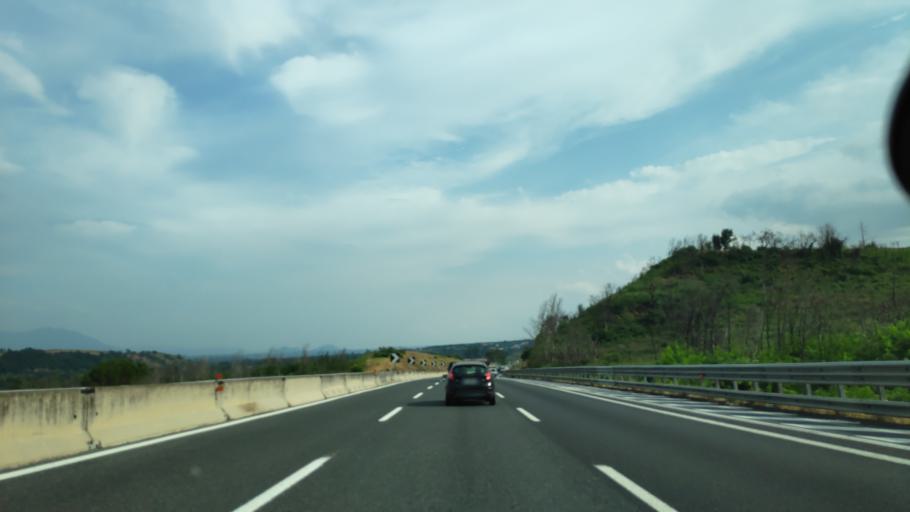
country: IT
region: Latium
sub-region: Citta metropolitana di Roma Capitale
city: Civitella San Paolo
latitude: 42.1982
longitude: 12.6034
